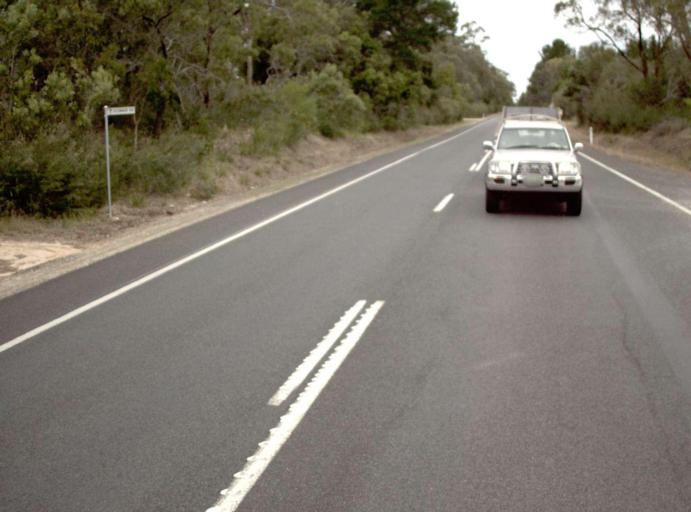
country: AU
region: Victoria
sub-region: Wellington
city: Sale
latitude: -38.1855
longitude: 147.0812
